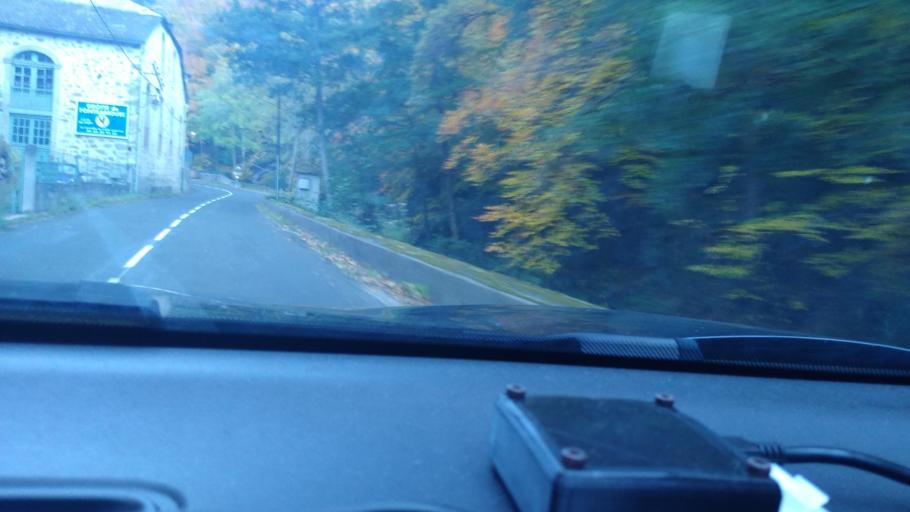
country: FR
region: Languedoc-Roussillon
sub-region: Departement de l'Aude
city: Quillan
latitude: 42.7192
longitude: 2.1226
